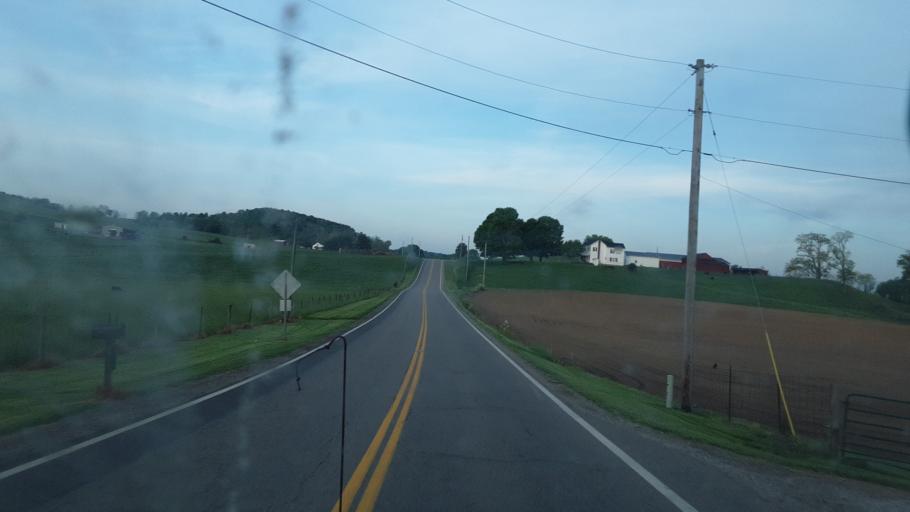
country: US
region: Ohio
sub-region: Ross County
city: Kingston
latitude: 39.4604
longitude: -82.7646
